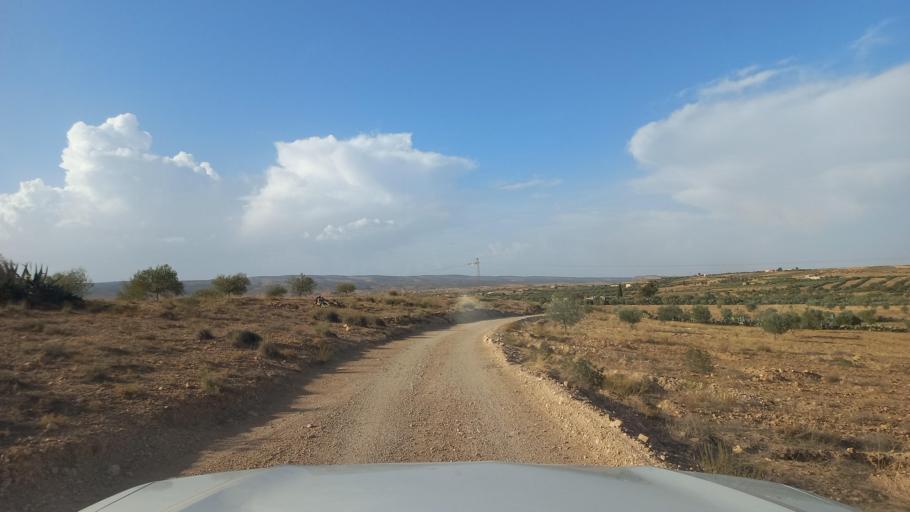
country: TN
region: Al Qasrayn
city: Kasserine
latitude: 35.2348
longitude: 8.9181
